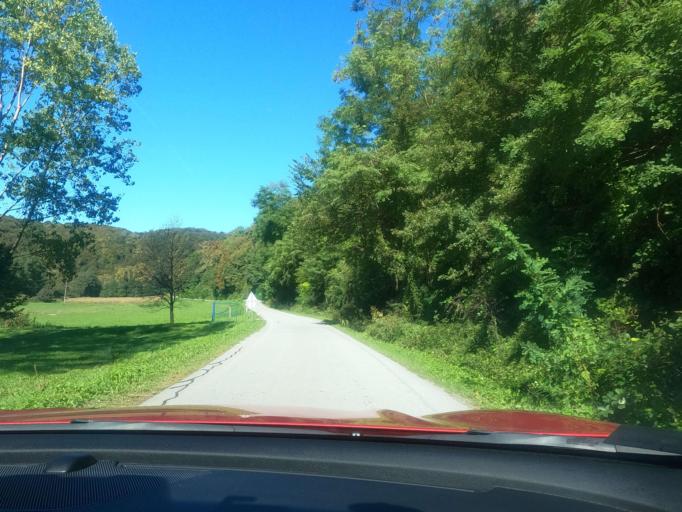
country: HR
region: Sisacko-Moslavacka
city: Petrinja
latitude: 45.3880
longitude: 16.2485
